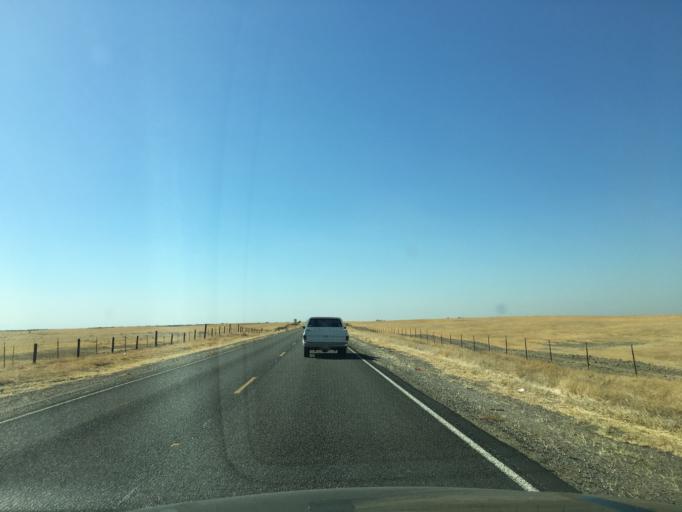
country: US
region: California
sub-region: Madera County
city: Bonadelle Ranchos-Madera Ranchos
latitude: 37.0103
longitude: -119.9086
